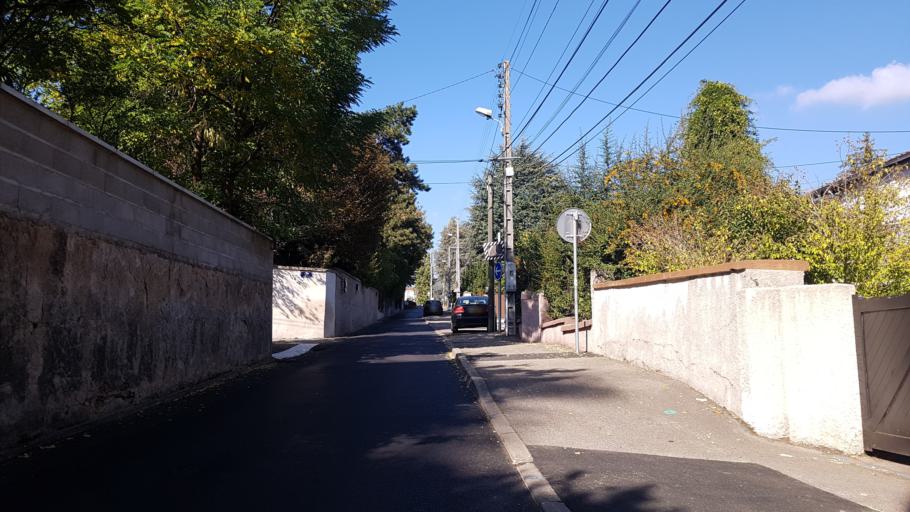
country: FR
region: Rhone-Alpes
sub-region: Departement du Rhone
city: Ecully
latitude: 45.7803
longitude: 4.7904
